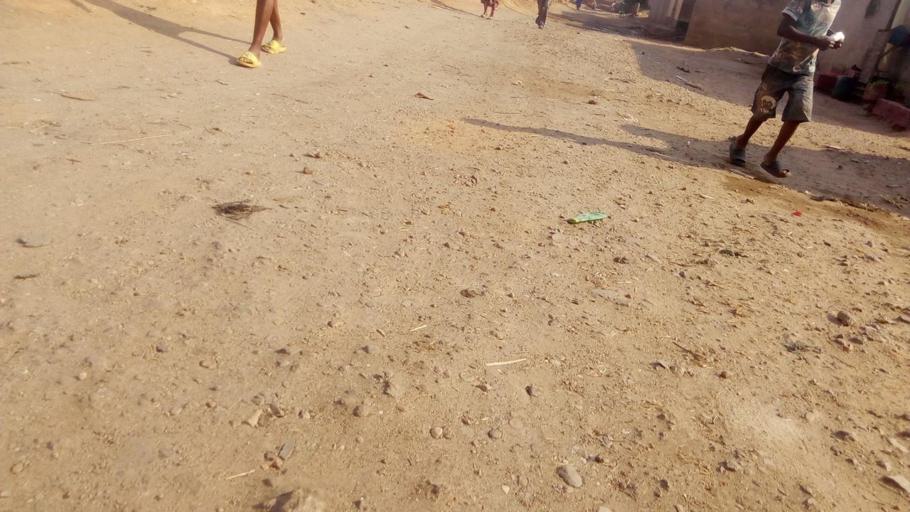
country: ZM
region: Lusaka
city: Lusaka
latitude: -15.3617
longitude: 28.2919
